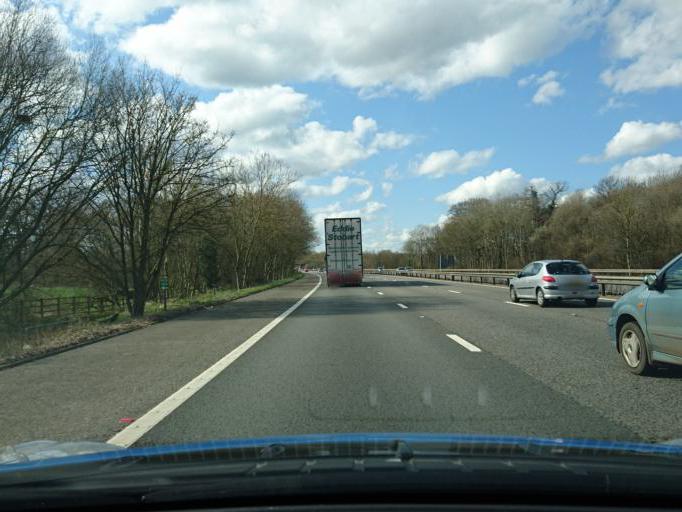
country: GB
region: England
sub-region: West Berkshire
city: Theale
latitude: 51.4540
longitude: -1.0820
